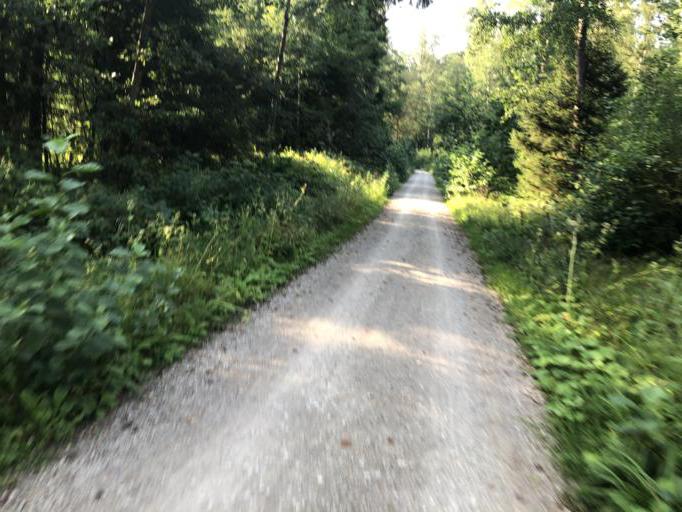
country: DE
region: Bavaria
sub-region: Regierungsbezirk Mittelfranken
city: Buckenhof
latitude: 49.5473
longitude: 11.0395
